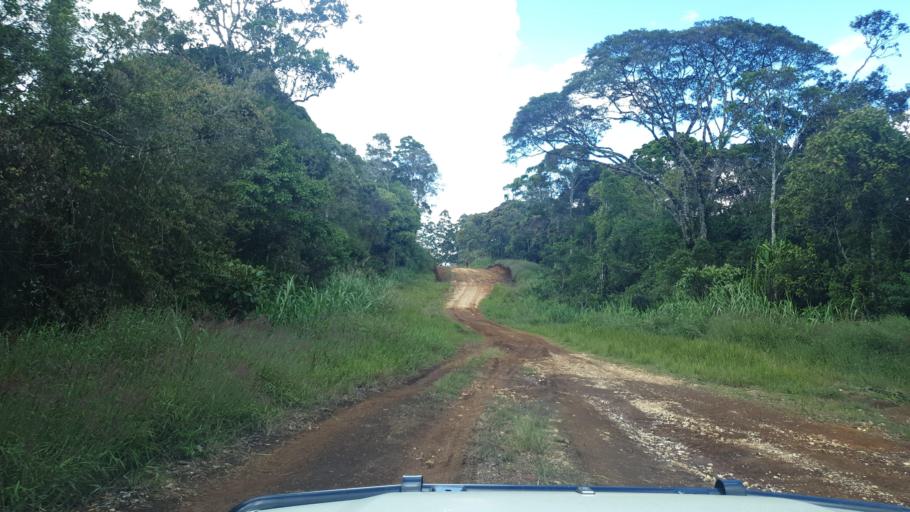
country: PG
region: Eastern Highlands
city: Goroka
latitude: -6.2792
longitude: 145.1954
